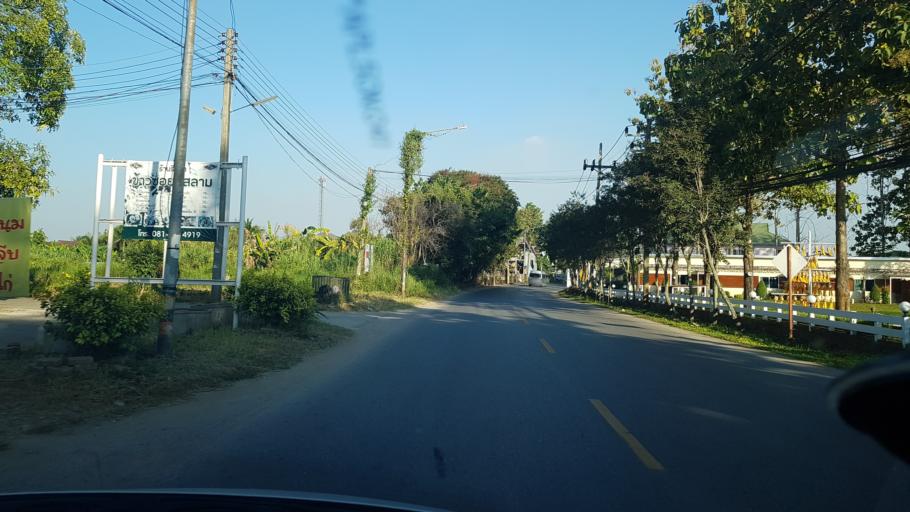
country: TH
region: Chiang Rai
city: Chiang Rai
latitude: 19.9290
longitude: 99.8300
